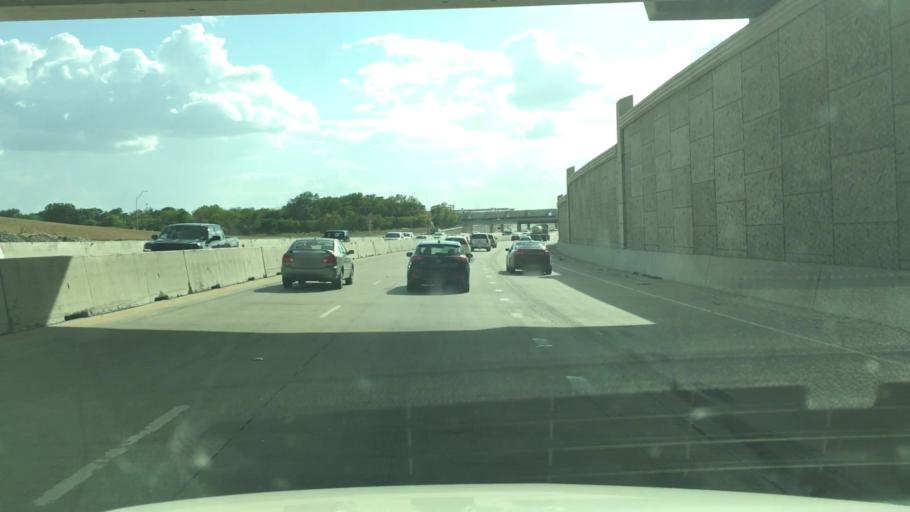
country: US
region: Texas
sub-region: Bell County
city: Temple
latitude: 31.1262
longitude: -97.3380
